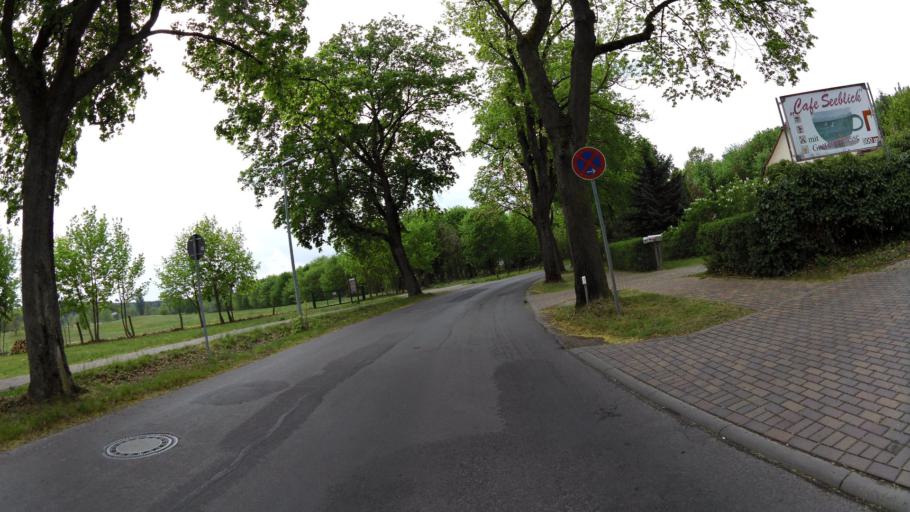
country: DE
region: Brandenburg
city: Schwerin
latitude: 52.2062
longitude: 13.5882
